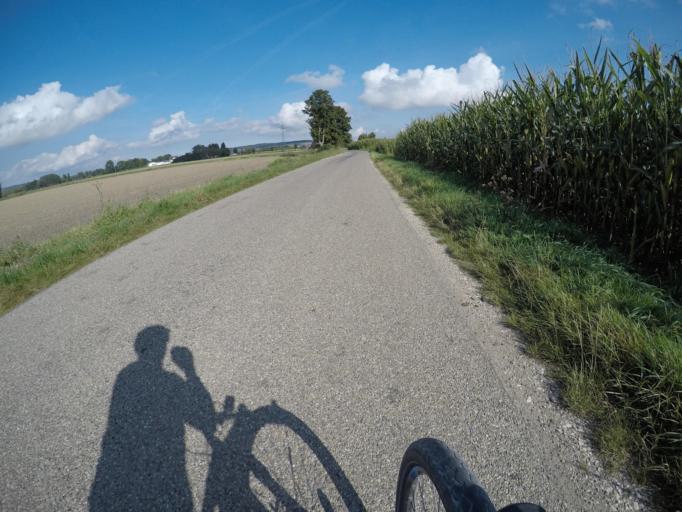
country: DE
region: Bavaria
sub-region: Swabia
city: Tapfheim
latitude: 48.6605
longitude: 10.7279
